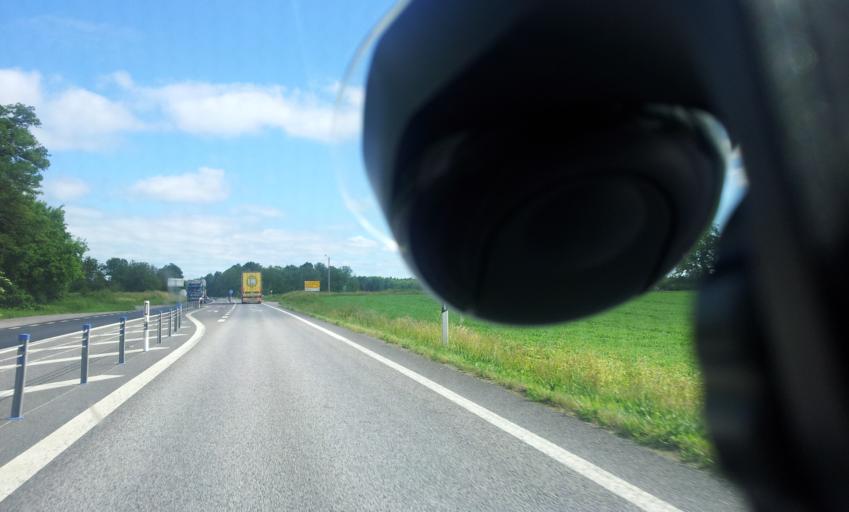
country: SE
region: Kalmar
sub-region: Kalmar Kommun
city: Lindsdal
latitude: 56.8090
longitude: 16.3675
